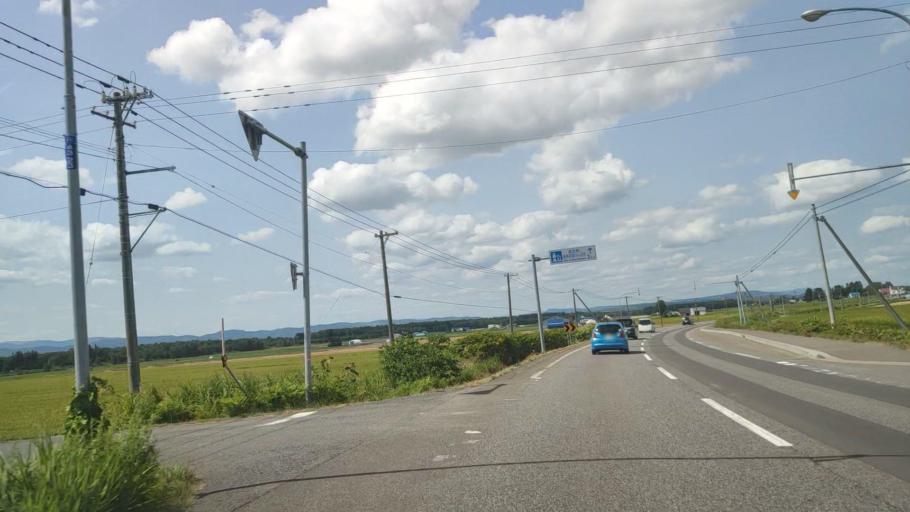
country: JP
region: Hokkaido
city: Nayoro
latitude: 44.0748
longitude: 142.3914
